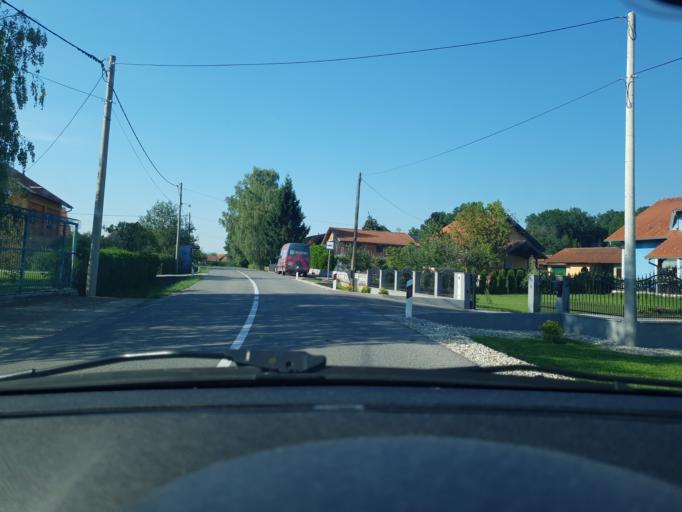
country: HR
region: Zagrebacka
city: Jakovlje
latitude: 45.9246
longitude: 15.8430
